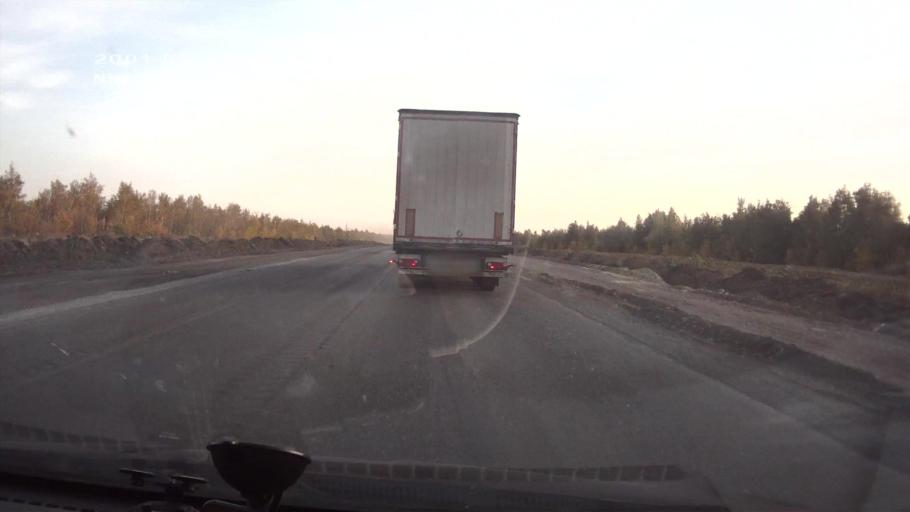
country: RU
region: Saratov
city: Kamenskiy
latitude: 50.9303
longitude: 45.5999
